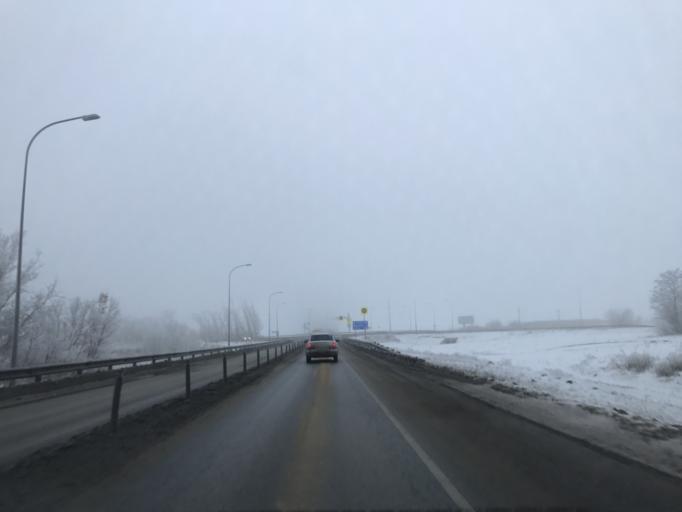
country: RU
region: Rostov
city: Temernik
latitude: 47.3696
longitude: 39.7874
